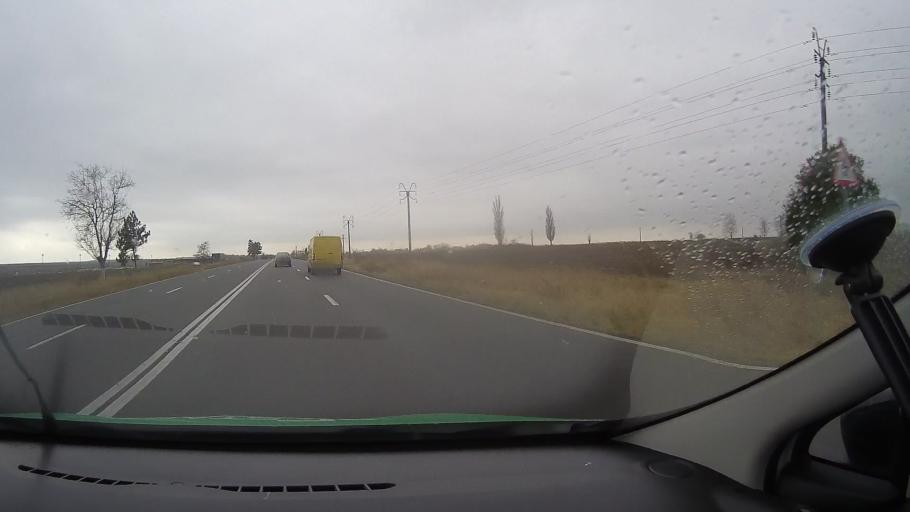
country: RO
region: Constanta
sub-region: Comuna Cumpana
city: Cumpana
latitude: 44.1659
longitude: 28.5319
